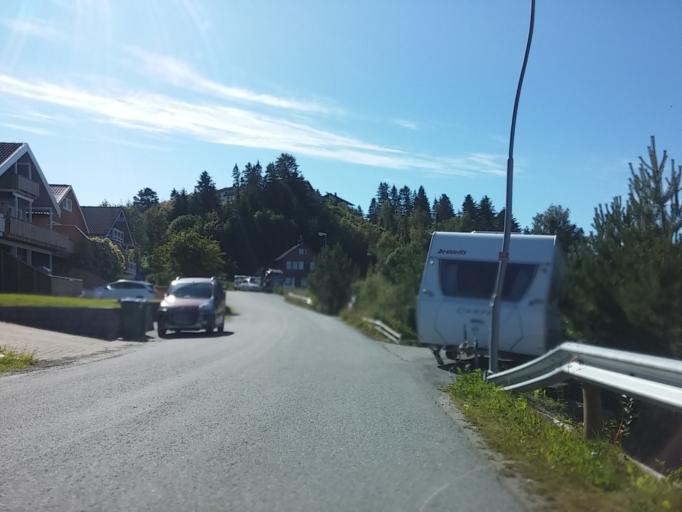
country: NO
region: Sor-Trondelag
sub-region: Malvik
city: Hommelvik
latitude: 63.4308
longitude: 10.7478
